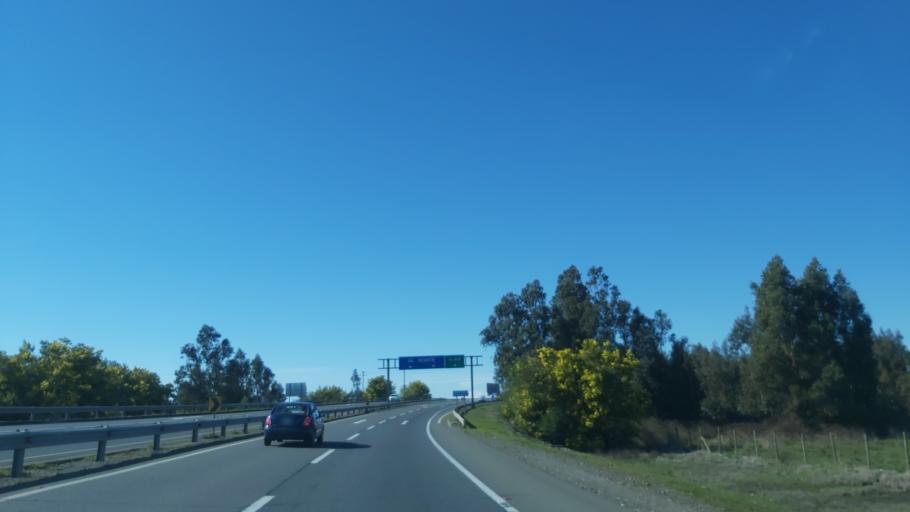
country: CL
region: Biobio
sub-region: Provincia de Nuble
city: Bulnes
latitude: -36.6538
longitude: -72.2355
